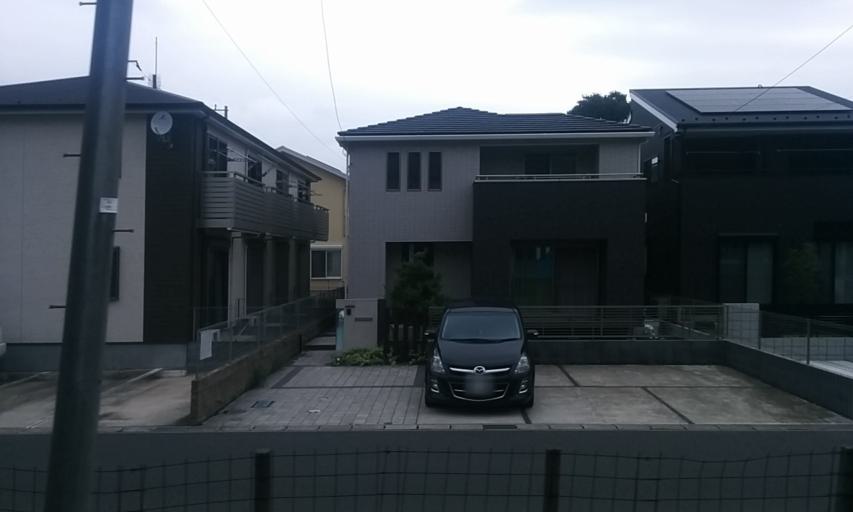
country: JP
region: Chiba
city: Nagareyama
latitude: 35.8442
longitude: 139.9074
